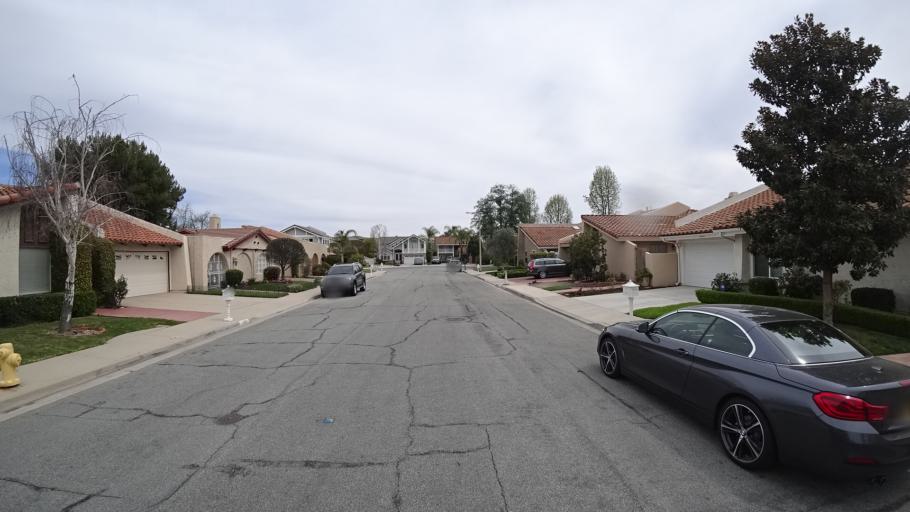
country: US
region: California
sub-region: Los Angeles County
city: Westlake Village
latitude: 34.1432
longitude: -118.8329
